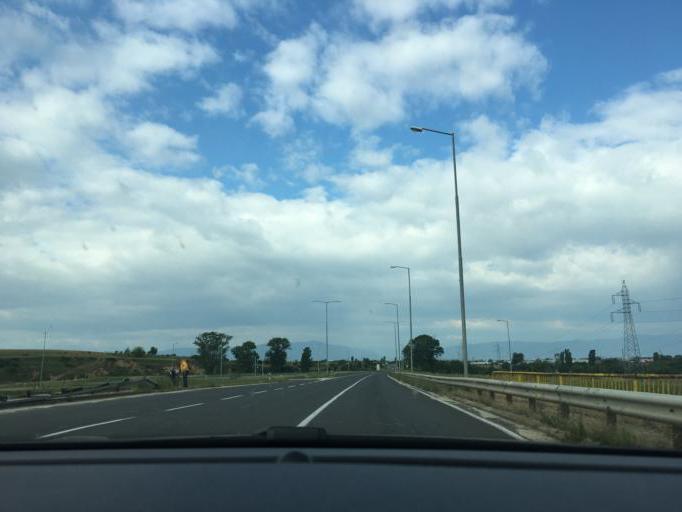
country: MK
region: Prilep
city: Prilep
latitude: 41.3303
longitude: 21.5579
